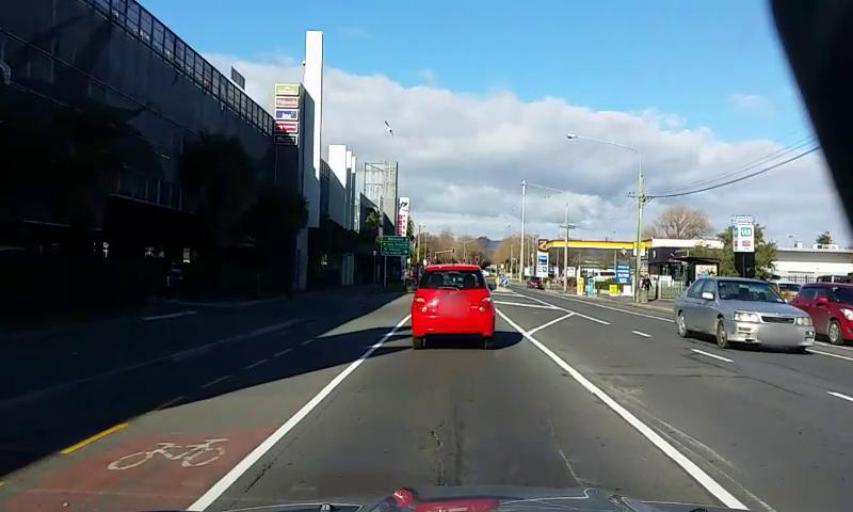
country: NZ
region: Canterbury
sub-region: Christchurch City
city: Christchurch
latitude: -43.5063
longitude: 172.6628
